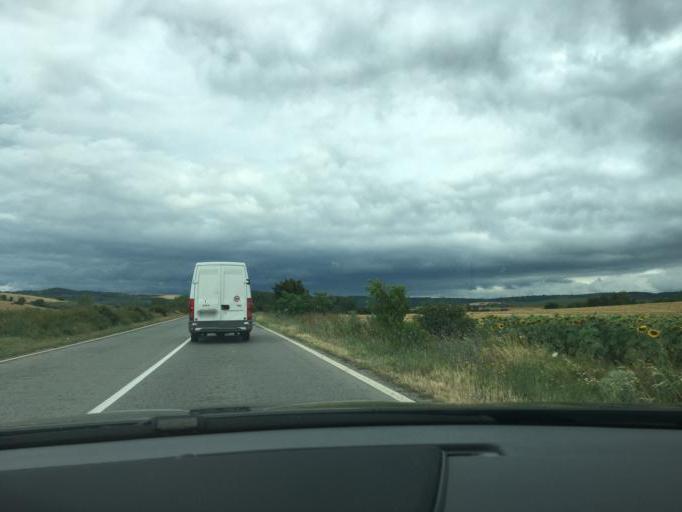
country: BG
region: Kyustendil
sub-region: Obshtina Bobovdol
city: Bobovdol
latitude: 42.2736
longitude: 23.0118
